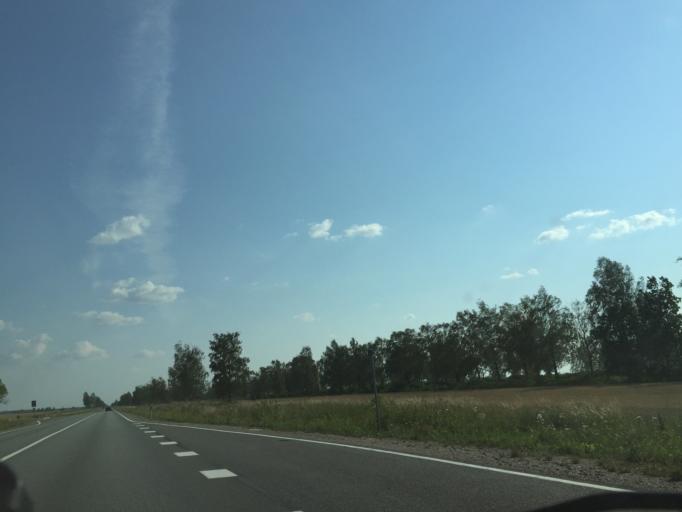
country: LV
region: Jelgava
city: Jelgava
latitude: 56.4825
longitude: 23.6964
